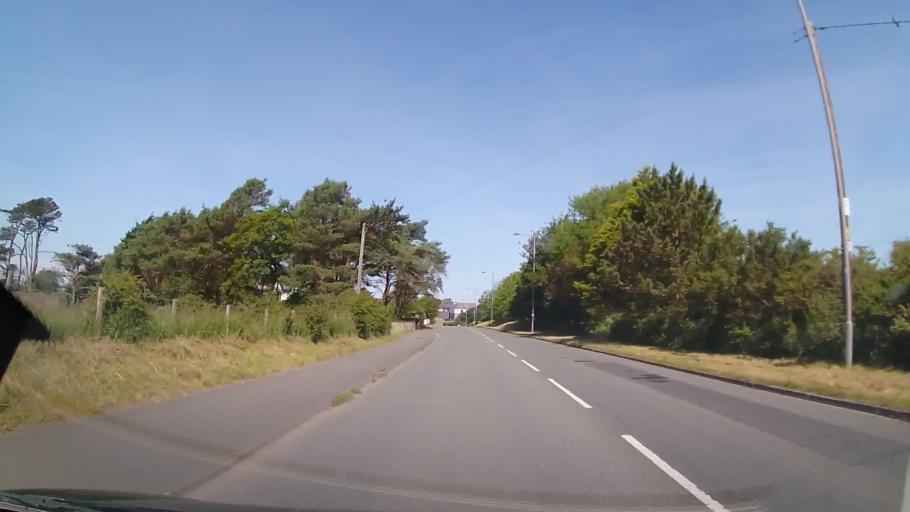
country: GB
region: Wales
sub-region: Gwynedd
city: Tywyn
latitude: 52.5813
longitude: -4.0770
